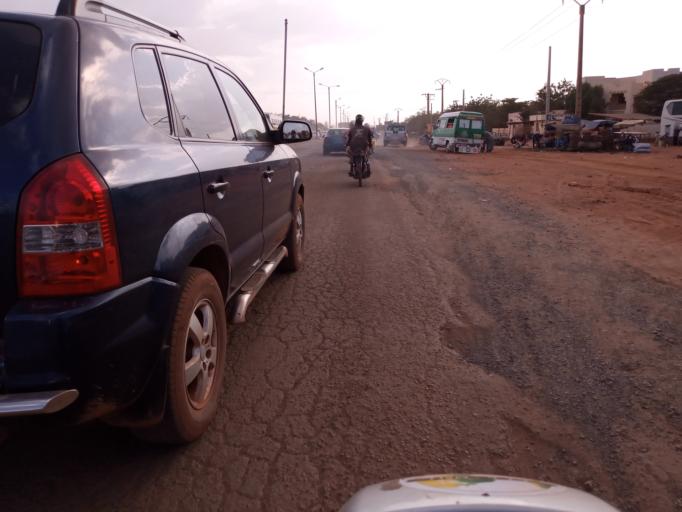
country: ML
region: Bamako
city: Bamako
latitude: 12.5933
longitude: -7.9405
